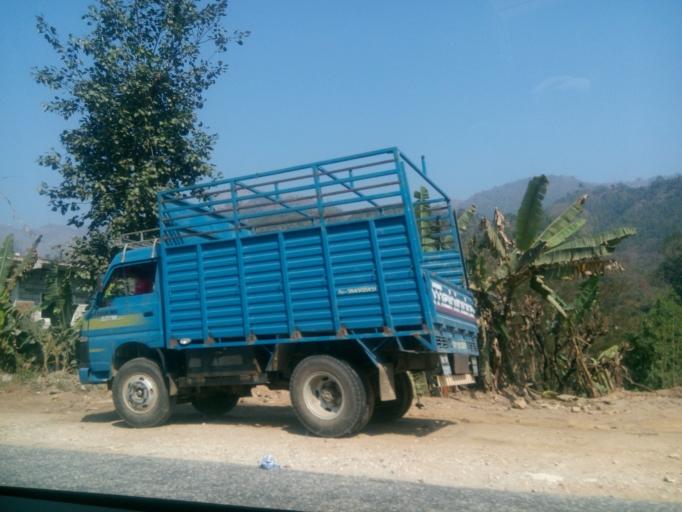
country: NP
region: Central Region
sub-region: Narayani Zone
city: Bharatpur
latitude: 27.8128
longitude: 84.8142
